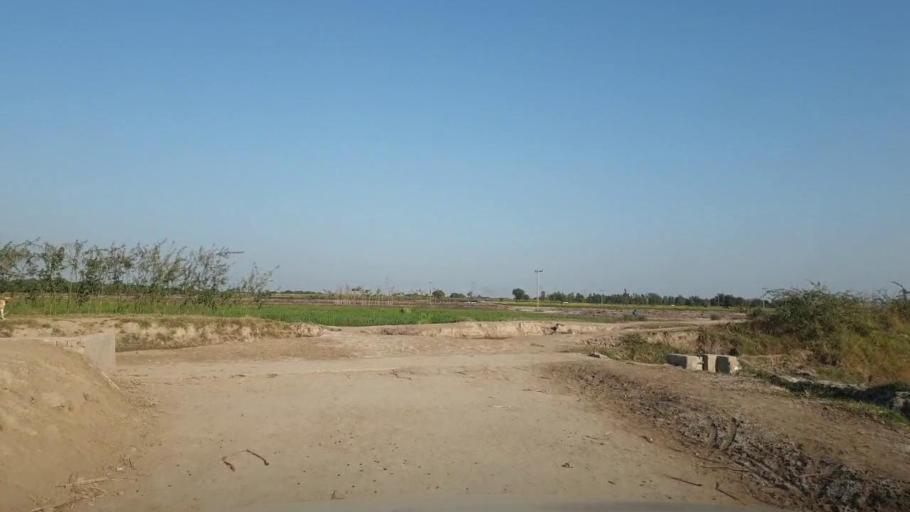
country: PK
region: Sindh
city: Tando Allahyar
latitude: 25.5066
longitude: 68.6630
